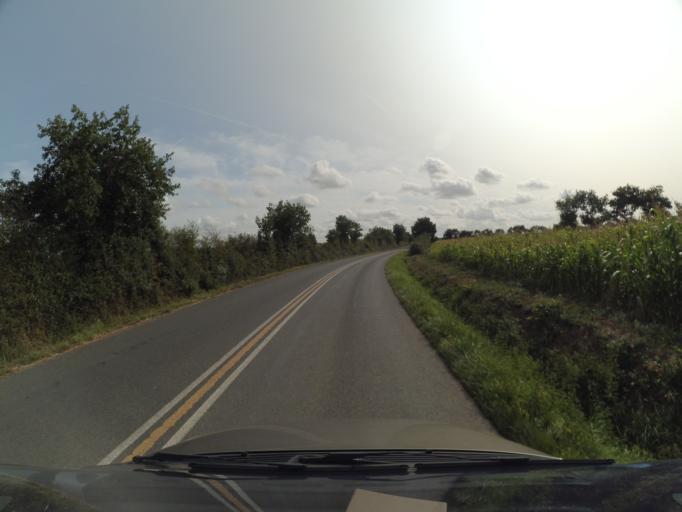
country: FR
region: Pays de la Loire
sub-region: Departement de la Vendee
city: La Guyonniere
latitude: 46.9747
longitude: -1.2421
